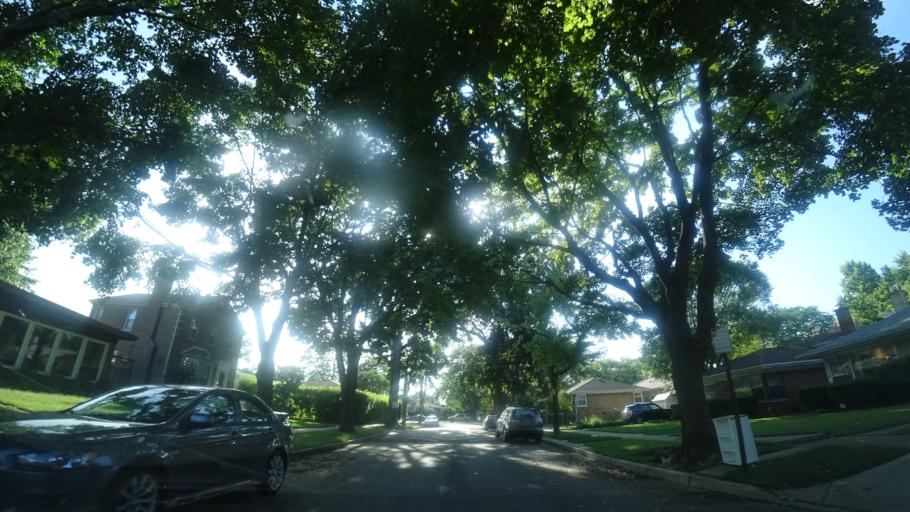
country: US
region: Illinois
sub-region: Cook County
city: Evanston
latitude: 42.0275
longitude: -87.6983
